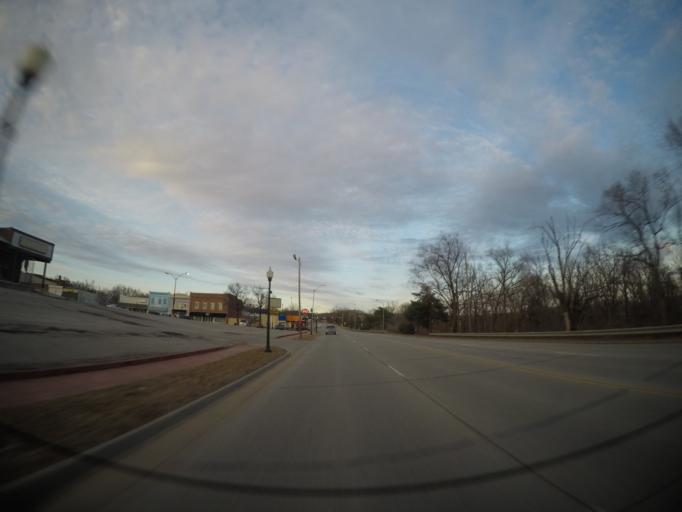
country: US
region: Kansas
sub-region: Wyandotte County
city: Bonner Springs
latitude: 39.0548
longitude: -94.8821
